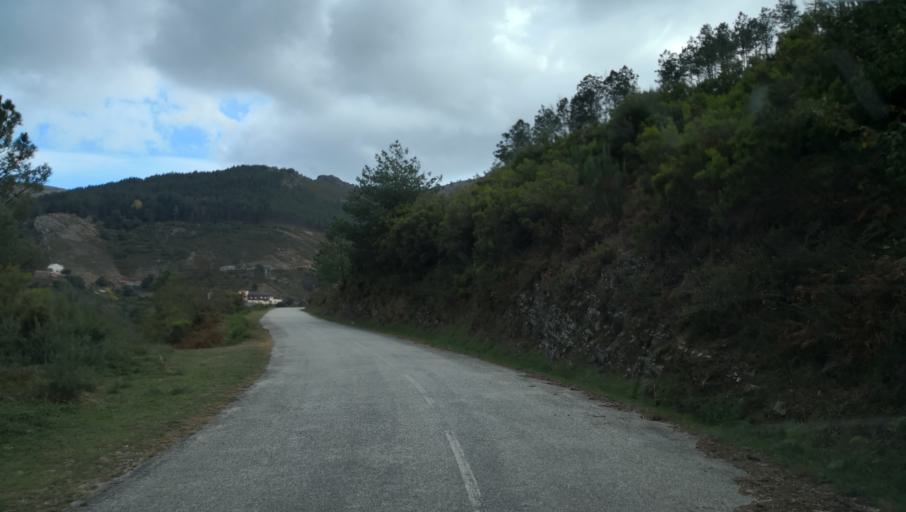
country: PT
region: Vila Real
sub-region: Mondim de Basto
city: Mondim de Basto
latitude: 41.3617
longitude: -7.8538
